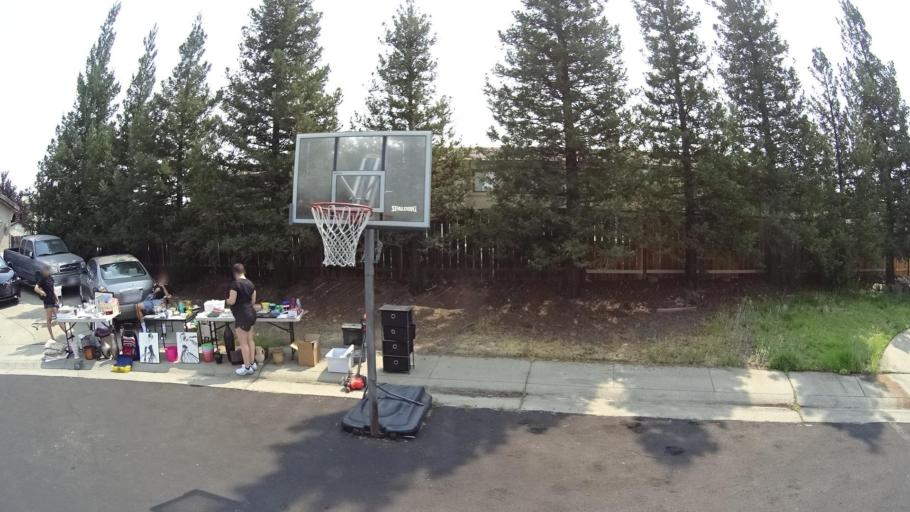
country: US
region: California
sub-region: Placer County
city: Rocklin
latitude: 38.7961
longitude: -121.2708
